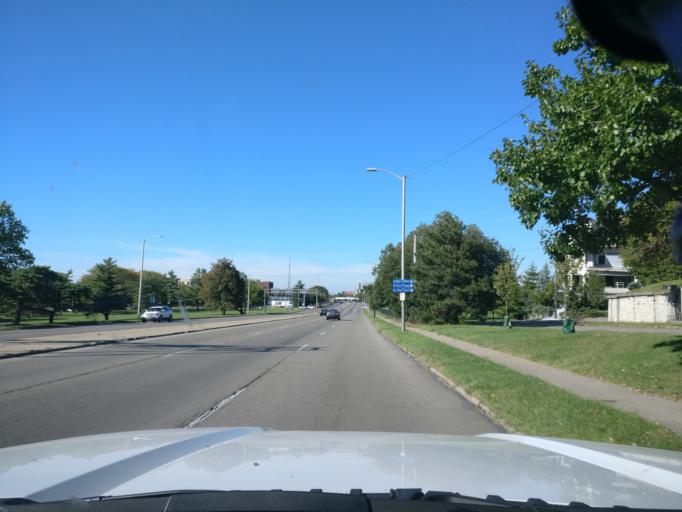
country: US
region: Ohio
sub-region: Montgomery County
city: Dayton
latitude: 39.7556
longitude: -84.1764
